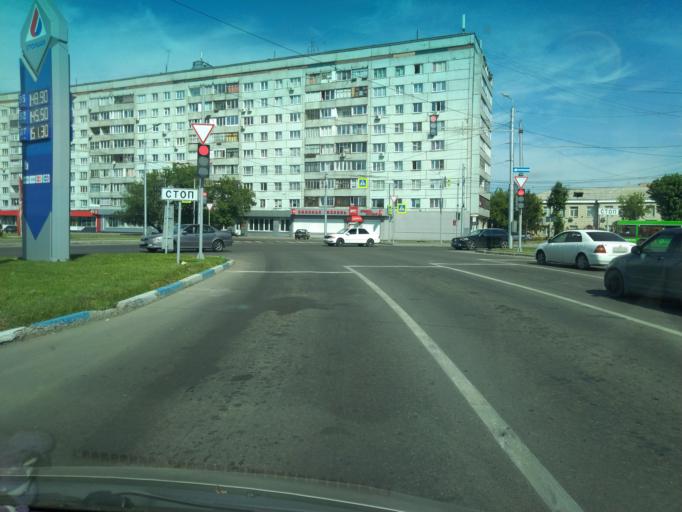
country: RU
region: Krasnoyarskiy
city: Krasnoyarsk
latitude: 56.0126
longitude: 92.8402
